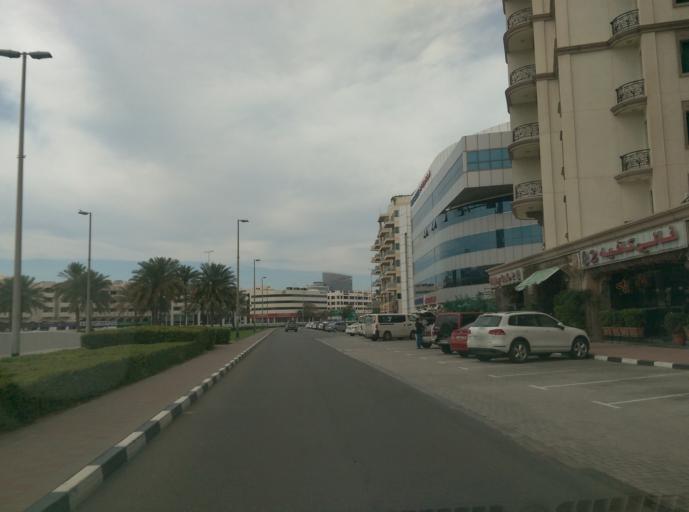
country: AE
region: Ash Shariqah
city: Sharjah
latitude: 25.2355
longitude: 55.3061
